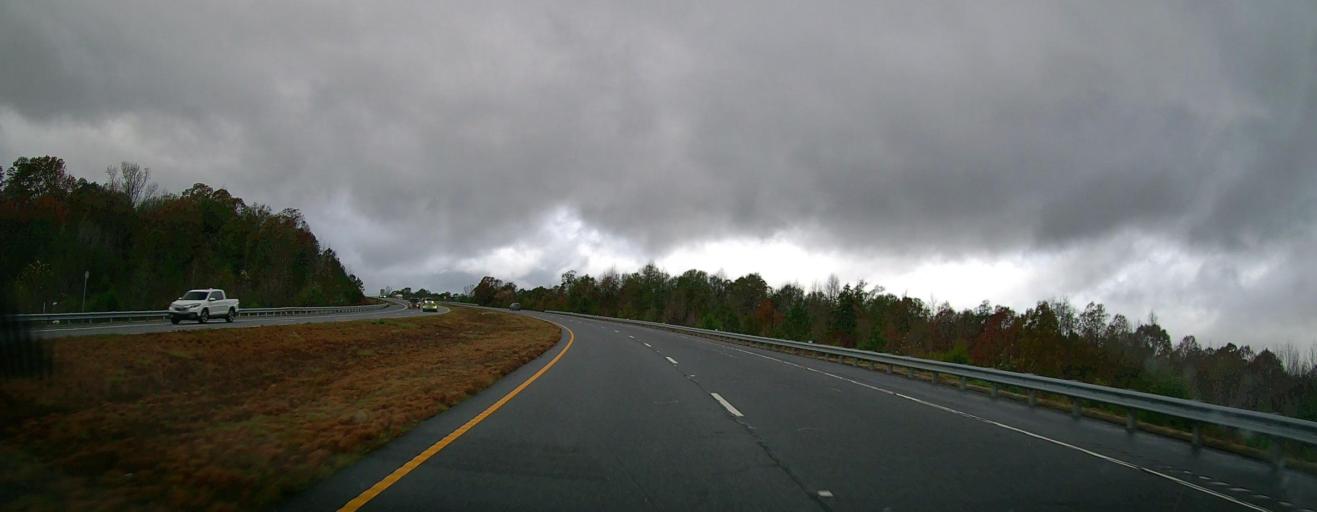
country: US
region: Georgia
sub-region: Jackson County
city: Nicholson
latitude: 34.0591
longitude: -83.4134
